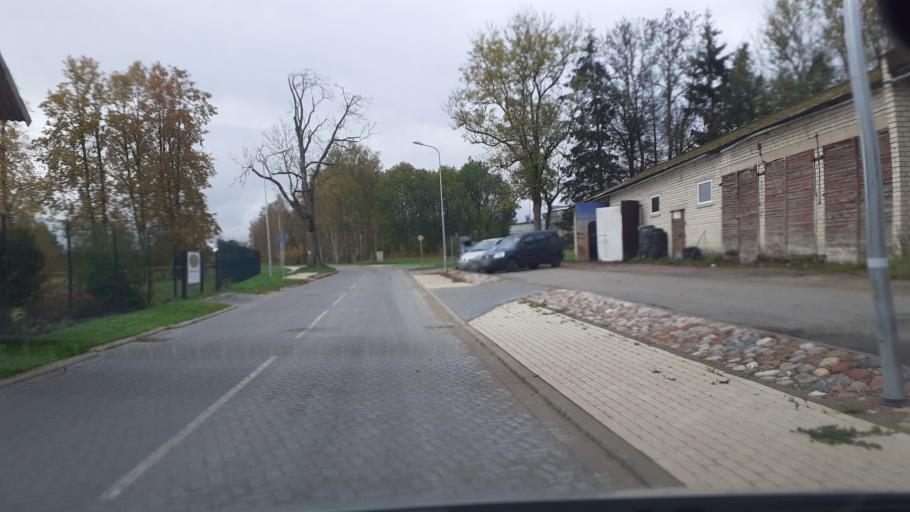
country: LV
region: Kuldigas Rajons
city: Kuldiga
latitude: 56.9865
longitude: 21.9497
